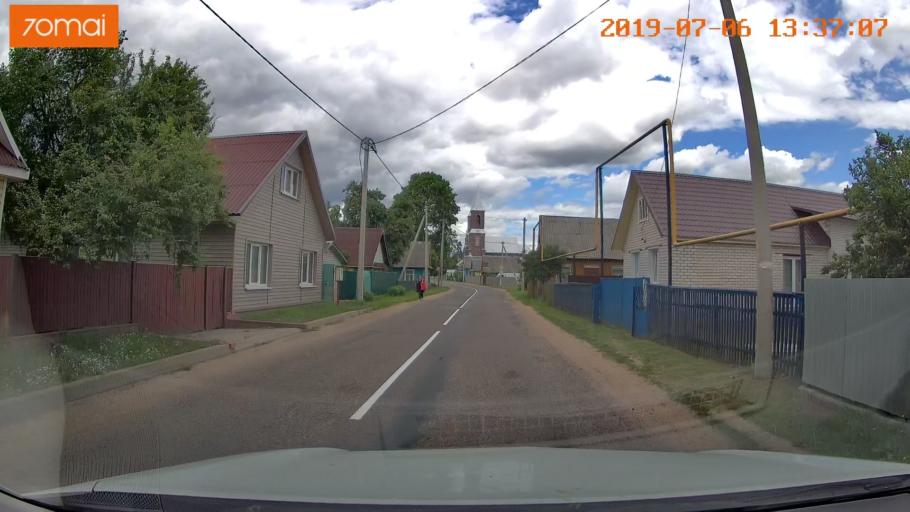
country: BY
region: Minsk
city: Enyerhyetykaw
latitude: 53.6923
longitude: 26.8668
